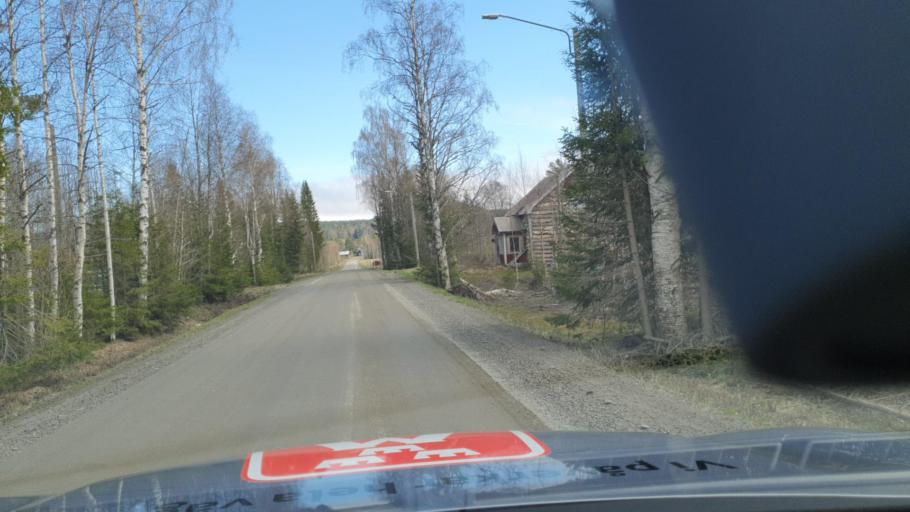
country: SE
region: Vaesterbotten
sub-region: Bjurholms Kommun
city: Bjurholm
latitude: 63.7001
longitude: 18.9341
